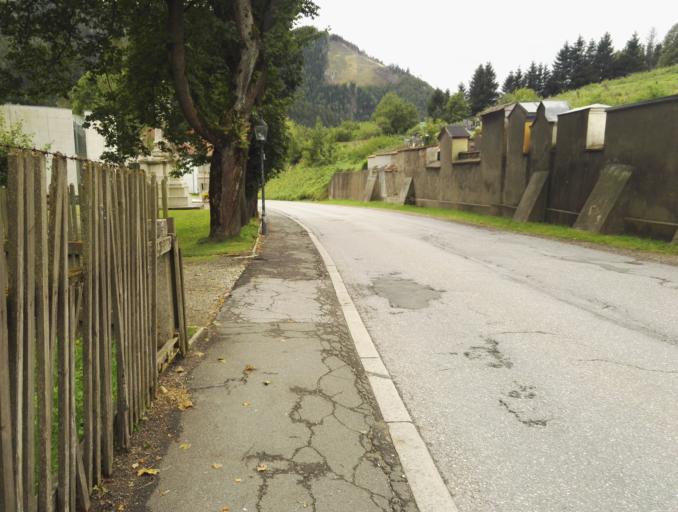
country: AT
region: Styria
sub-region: Politischer Bezirk Leoben
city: Vordernberg
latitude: 47.4917
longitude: 14.9930
